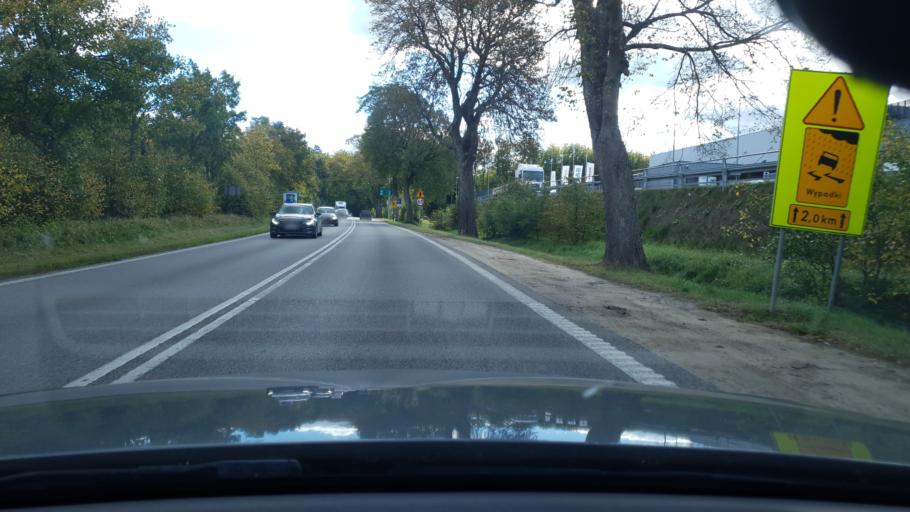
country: PL
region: Pomeranian Voivodeship
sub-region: Powiat wejherowski
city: Rekowo Dolne
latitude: 54.6357
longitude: 18.3451
